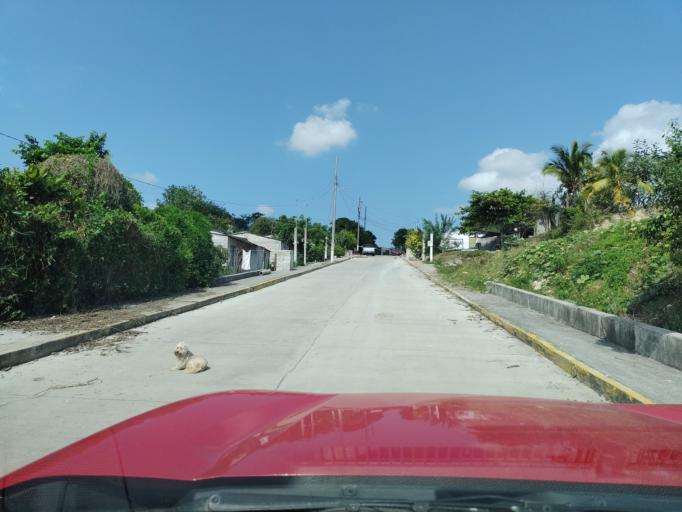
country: MX
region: Veracruz
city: Agua Dulce
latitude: 20.3041
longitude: -97.1734
